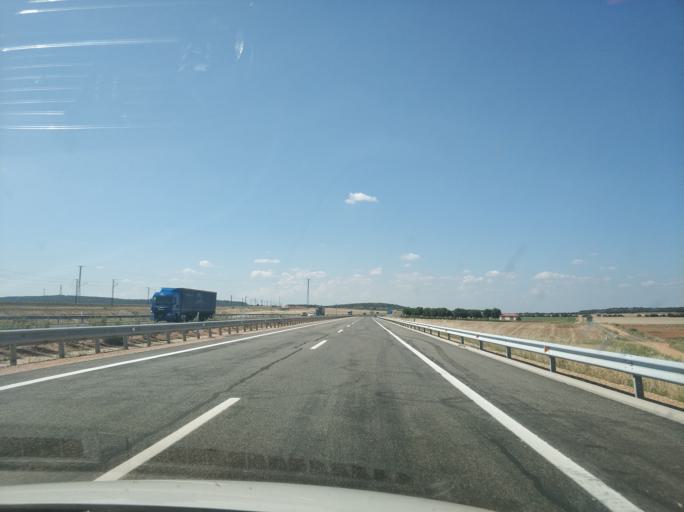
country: ES
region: Castille and Leon
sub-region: Provincia de Zamora
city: Montamarta
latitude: 41.6696
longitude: -5.8016
